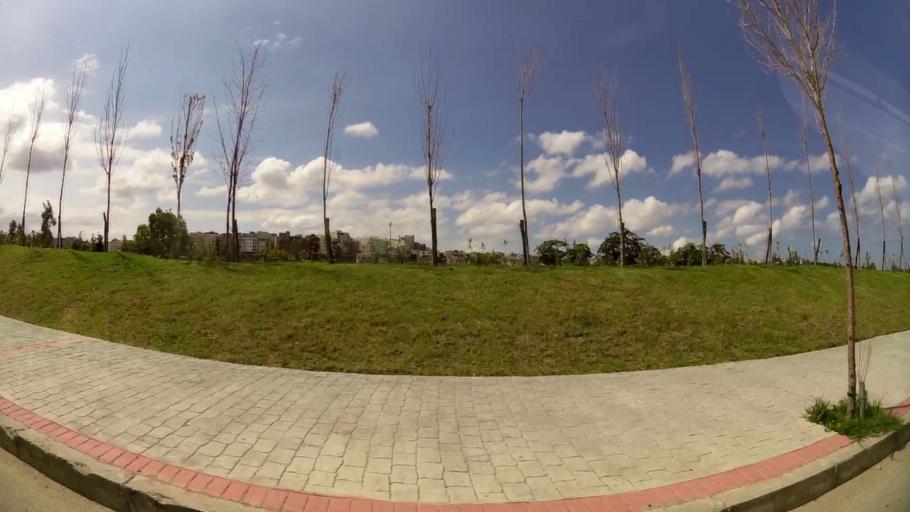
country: MA
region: Tanger-Tetouan
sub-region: Tanger-Assilah
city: Tangier
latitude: 35.7741
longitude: -5.7618
